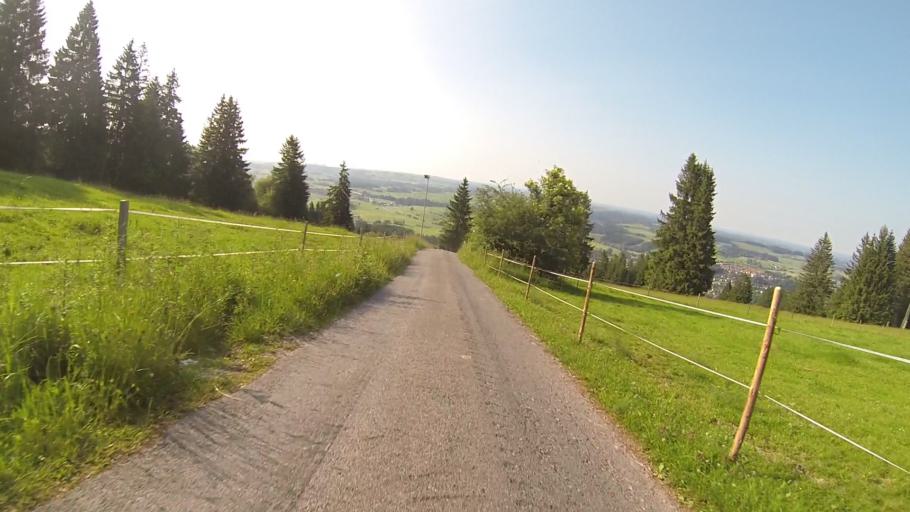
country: DE
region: Bavaria
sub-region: Swabia
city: Nesselwang
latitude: 47.6095
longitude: 10.4986
